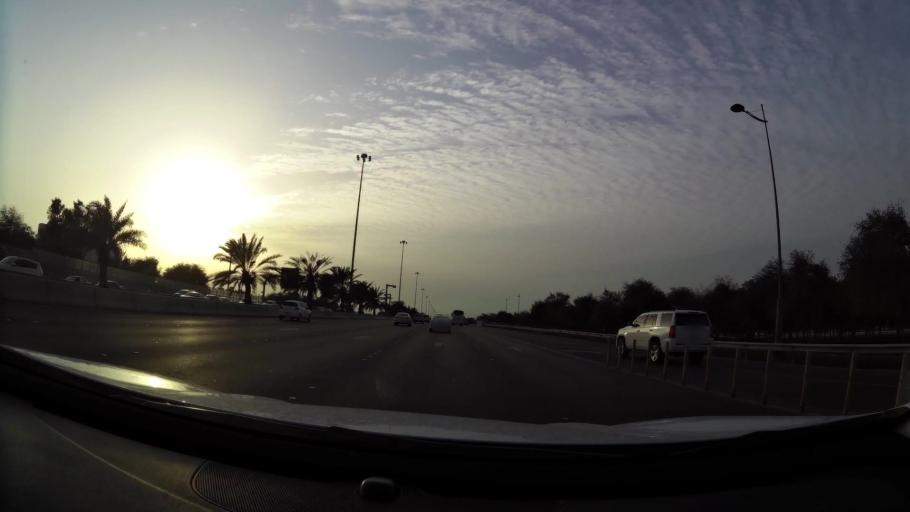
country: AE
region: Abu Dhabi
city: Abu Dhabi
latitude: 24.3987
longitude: 54.5039
